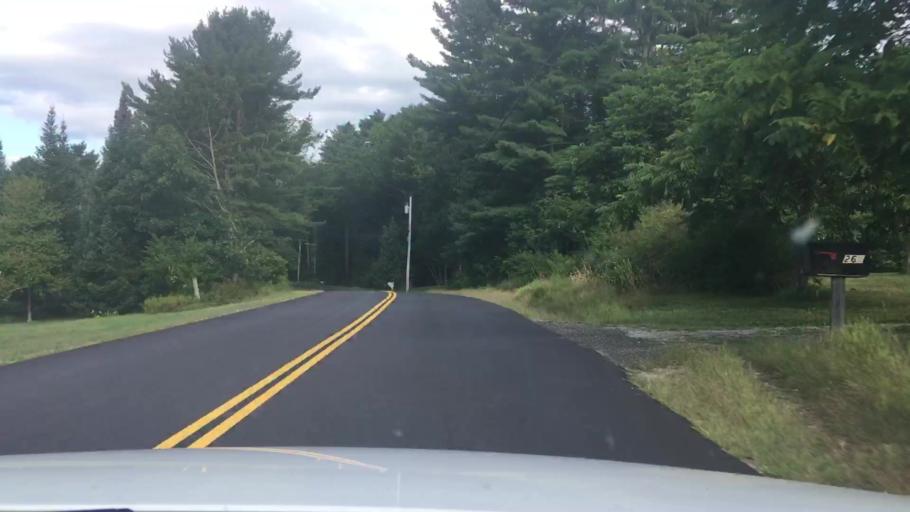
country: US
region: Maine
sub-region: Androscoggin County
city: Lisbon Falls
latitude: 44.0421
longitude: -70.0420
